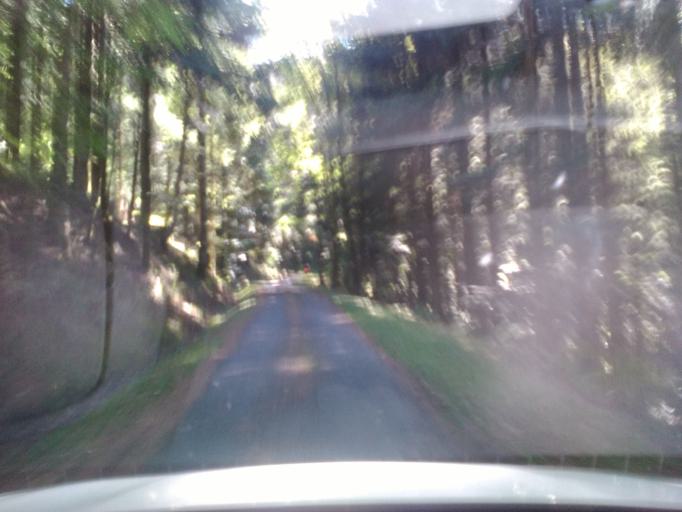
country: FR
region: Lorraine
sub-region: Departement des Vosges
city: Sainte-Marguerite
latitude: 48.3121
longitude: 6.9948
